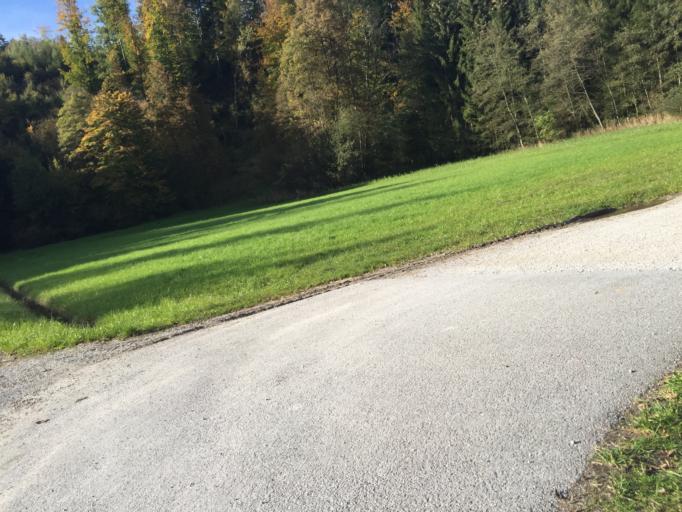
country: AT
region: Salzburg
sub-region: Politischer Bezirk Salzburg-Umgebung
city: Grodig
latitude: 47.7544
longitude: 12.9950
